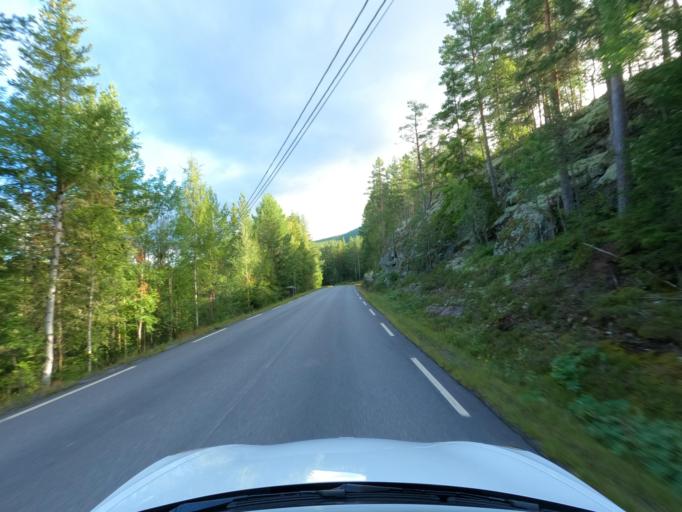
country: NO
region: Telemark
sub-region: Hjartdal
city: Sauland
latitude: 59.7869
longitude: 9.1021
